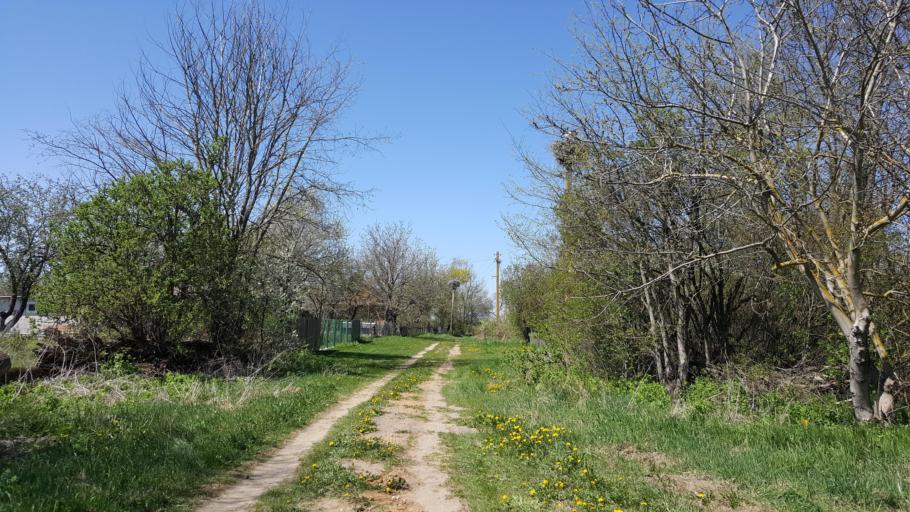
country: BY
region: Brest
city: Charnawchytsy
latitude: 52.3178
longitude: 23.7247
